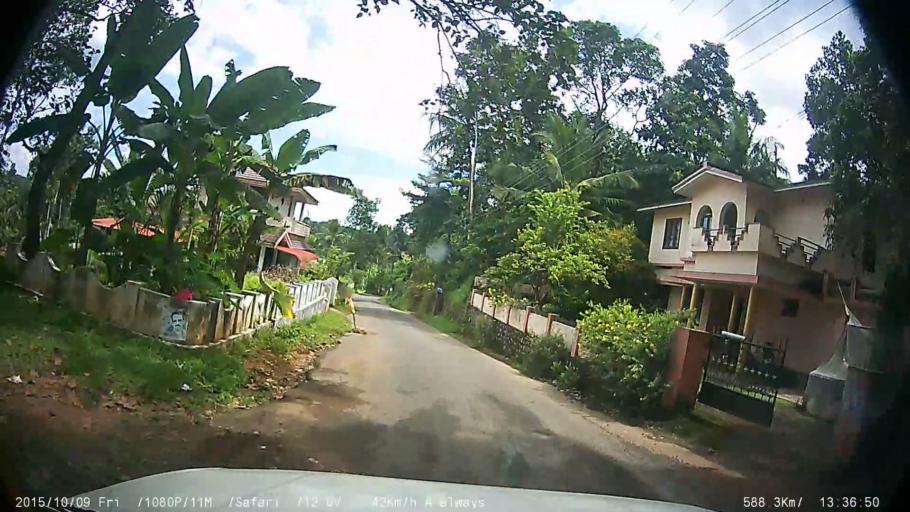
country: IN
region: Kerala
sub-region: Ernakulam
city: Piravam
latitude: 9.8966
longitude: 76.5623
